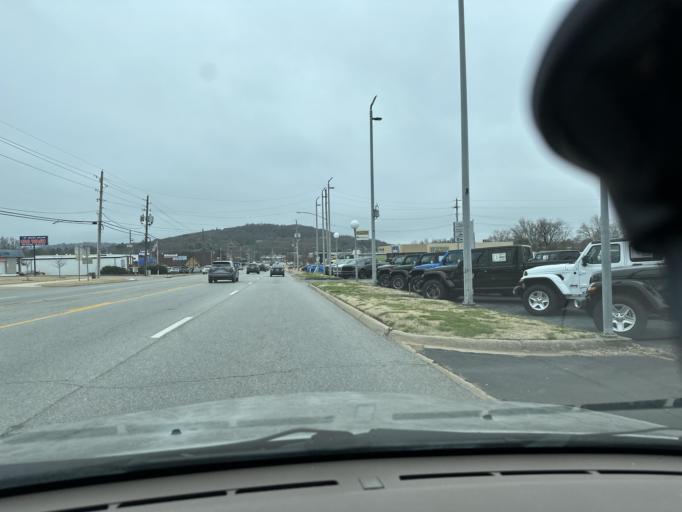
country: US
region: Arkansas
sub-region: Washington County
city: Johnson
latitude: 36.1121
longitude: -94.1452
